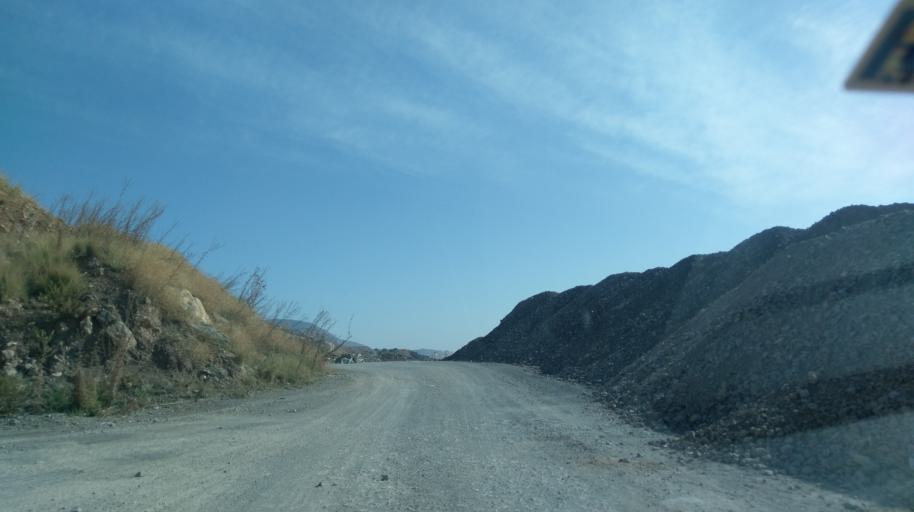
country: CY
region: Lefkosia
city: Nicosia
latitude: 35.2689
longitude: 33.4426
